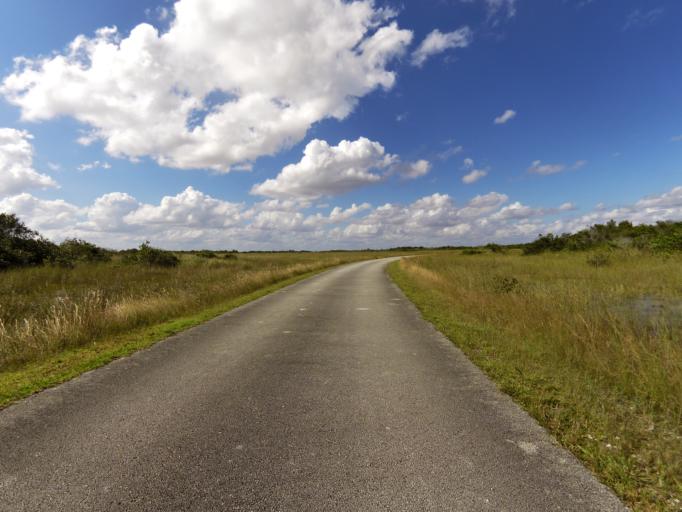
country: US
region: Florida
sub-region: Miami-Dade County
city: The Hammocks
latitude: 25.7180
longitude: -80.7620
